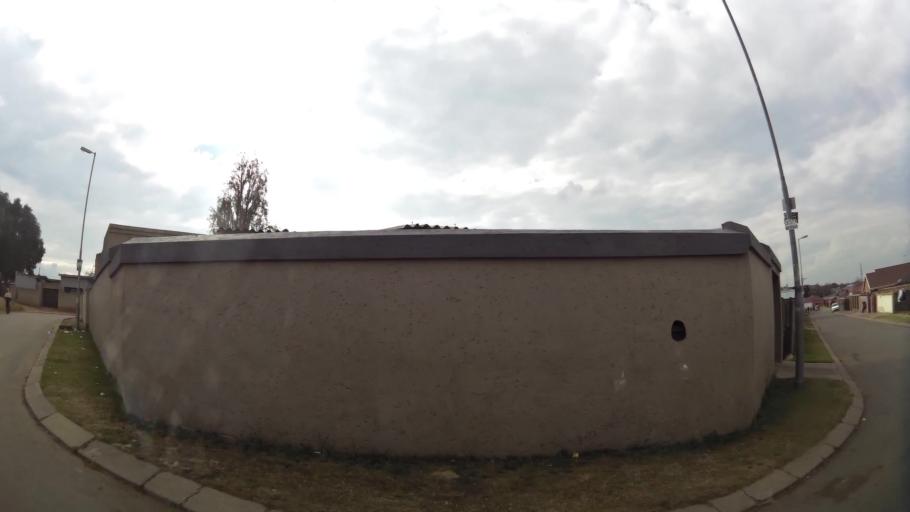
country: ZA
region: Gauteng
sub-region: City of Johannesburg Metropolitan Municipality
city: Soweto
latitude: -26.2389
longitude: 27.8615
